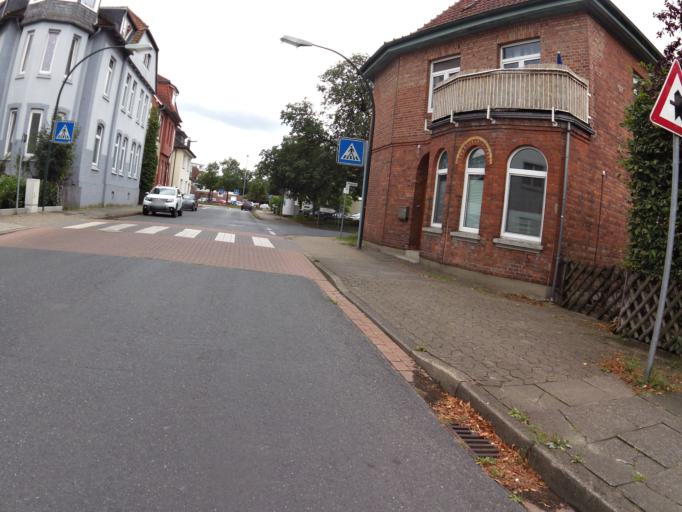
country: DE
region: Lower Saxony
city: Rotenburg
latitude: 53.1130
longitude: 9.4096
